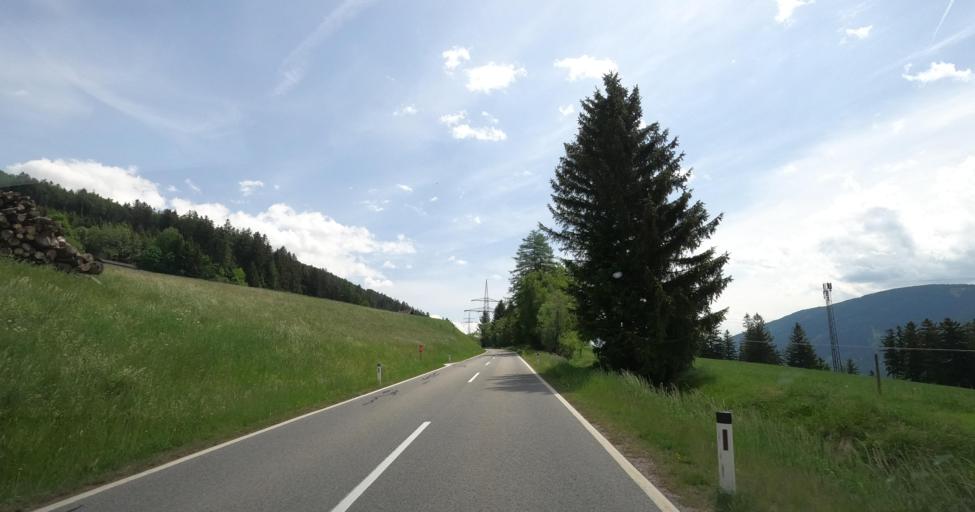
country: AT
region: Tyrol
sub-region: Politischer Bezirk Innsbruck Land
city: Patsch
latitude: 47.2003
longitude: 11.4198
